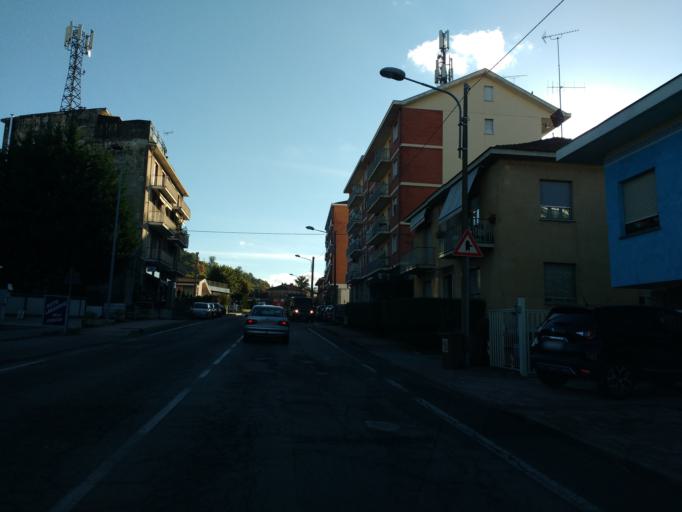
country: IT
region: Piedmont
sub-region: Provincia di Torino
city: Gassino Torinese
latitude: 45.1271
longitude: 7.8219
